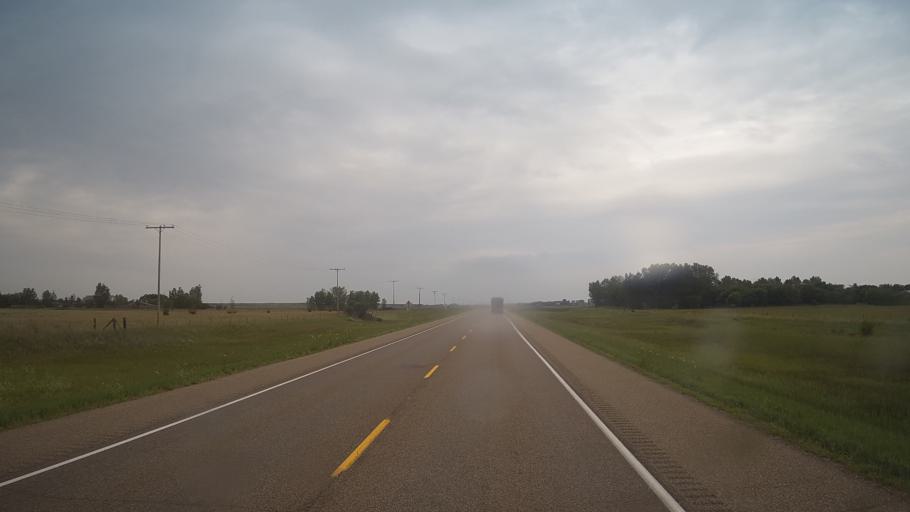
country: CA
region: Saskatchewan
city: Langham
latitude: 52.1289
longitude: -107.1392
